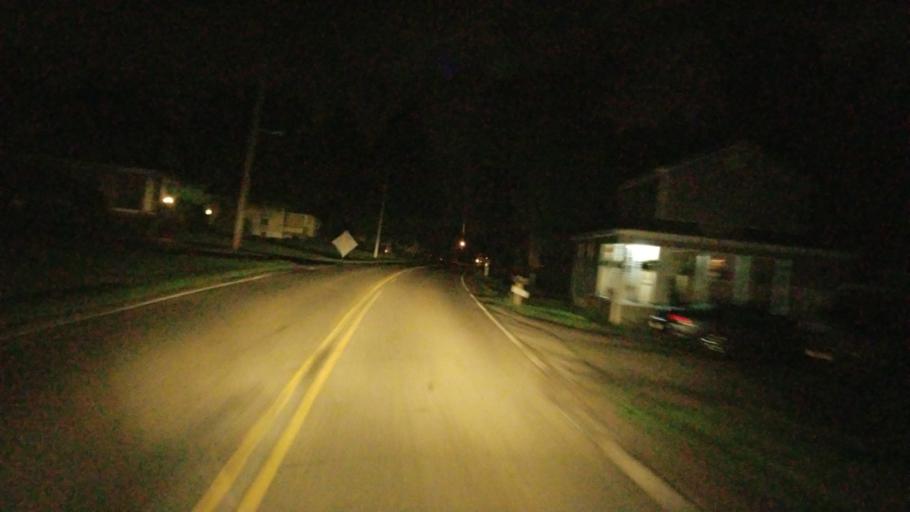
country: US
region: Ohio
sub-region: Trumbull County
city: Mineral Ridge
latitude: 41.1536
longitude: -80.7590
